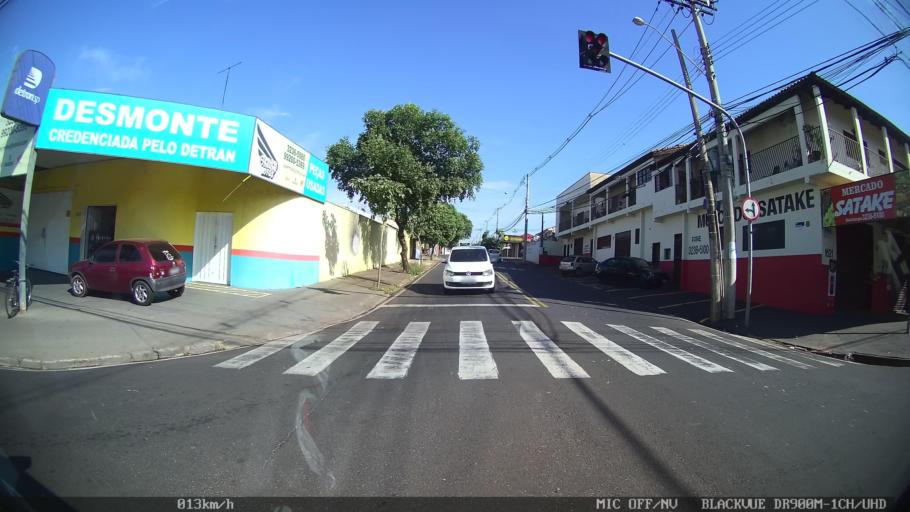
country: BR
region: Sao Paulo
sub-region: Sao Jose Do Rio Preto
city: Sao Jose do Rio Preto
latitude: -20.7744
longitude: -49.3855
